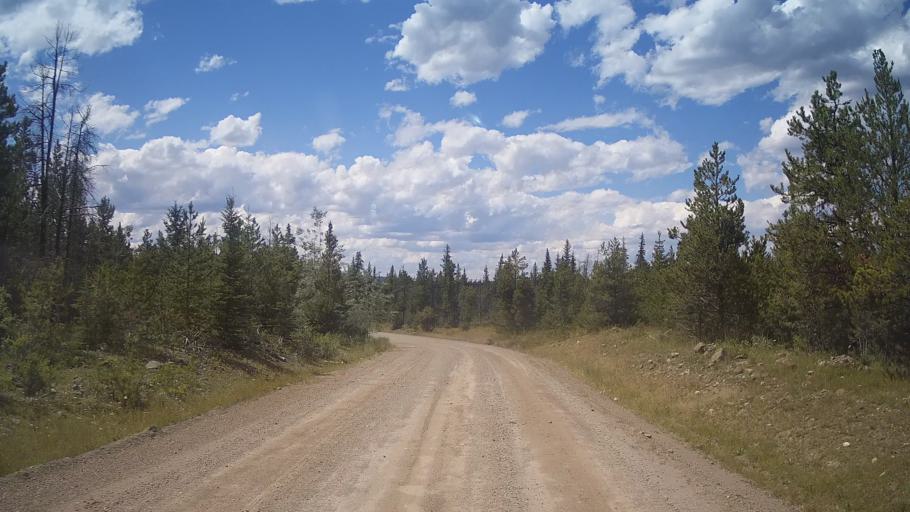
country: CA
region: British Columbia
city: Lillooet
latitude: 51.3398
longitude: -121.9497
